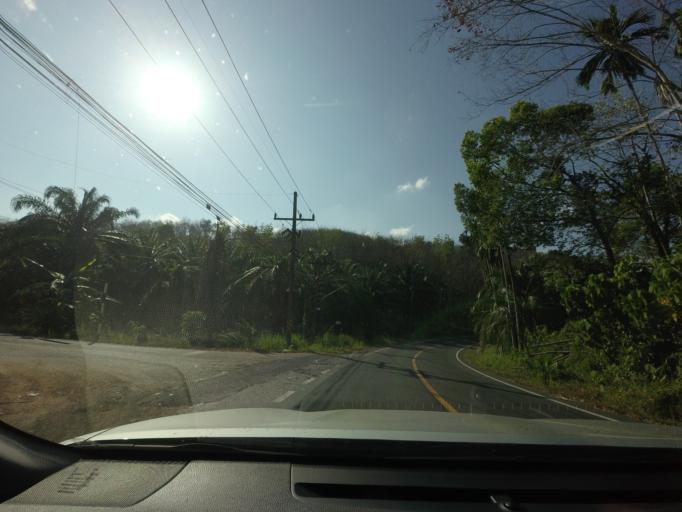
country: TH
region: Phangnga
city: Takua Thung
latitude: 8.2536
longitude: 98.3768
